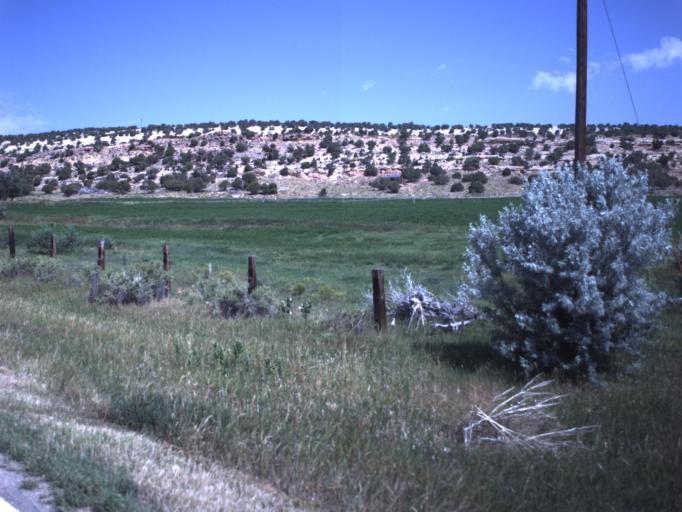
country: US
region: Utah
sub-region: Daggett County
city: Manila
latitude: 40.9759
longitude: -109.7695
